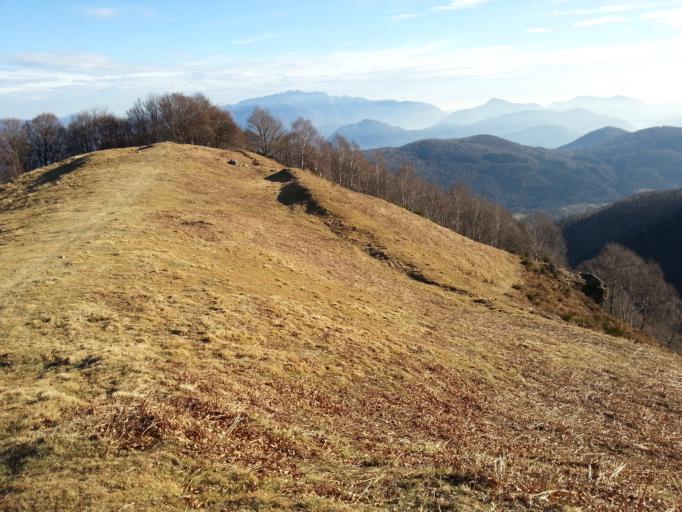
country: CH
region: Ticino
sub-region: Lugano District
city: Gravesano
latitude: 46.0579
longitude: 8.8743
